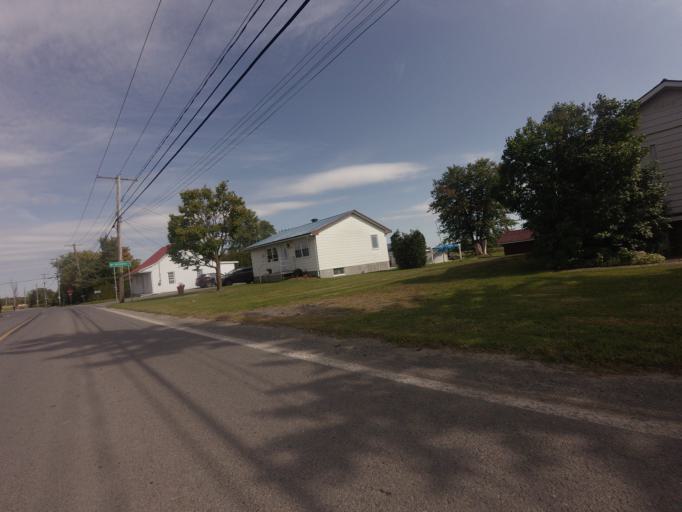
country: CA
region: Quebec
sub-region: Laurentides
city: Saint-Eustache
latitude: 45.6161
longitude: -73.9036
